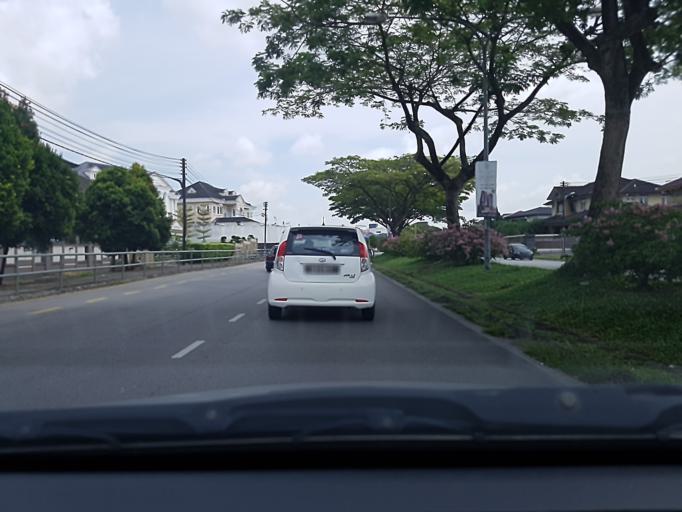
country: MY
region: Sarawak
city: Kuching
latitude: 1.5180
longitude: 110.3626
